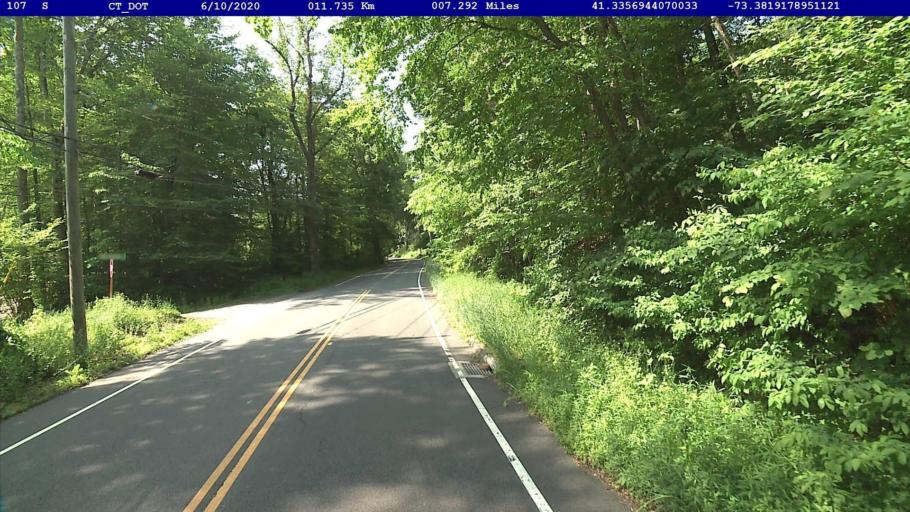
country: US
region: Connecticut
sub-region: Fairfield County
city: Bethel
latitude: 41.3361
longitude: -73.3819
